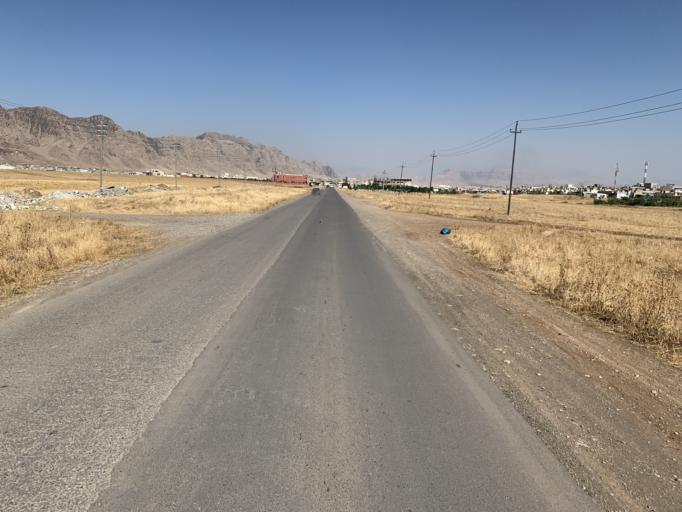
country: IQ
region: As Sulaymaniyah
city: Raniye
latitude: 36.2633
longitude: 44.8486
